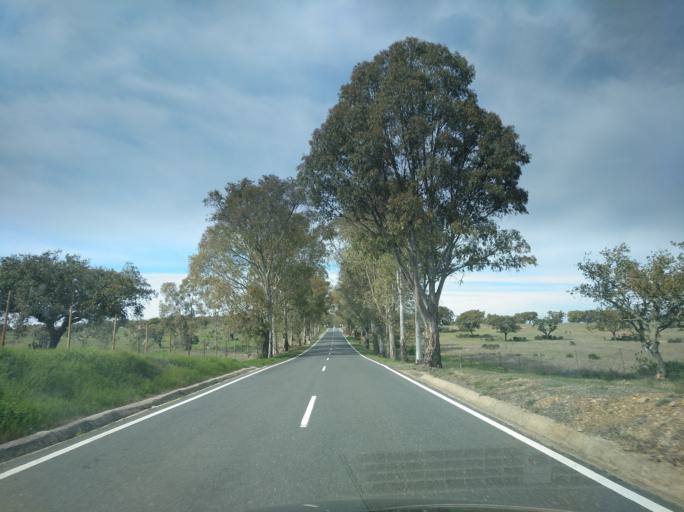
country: PT
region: Beja
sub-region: Mertola
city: Mertola
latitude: 37.7302
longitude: -7.7675
